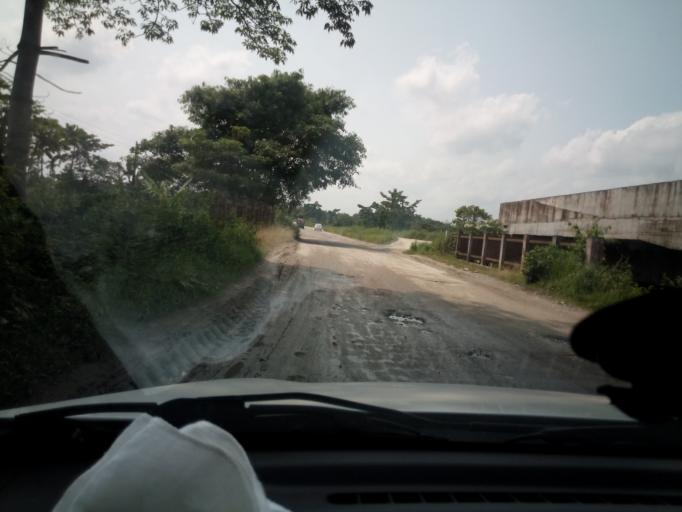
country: IN
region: Assam
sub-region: Udalguri
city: Udalguri
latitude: 26.7429
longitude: 92.1578
